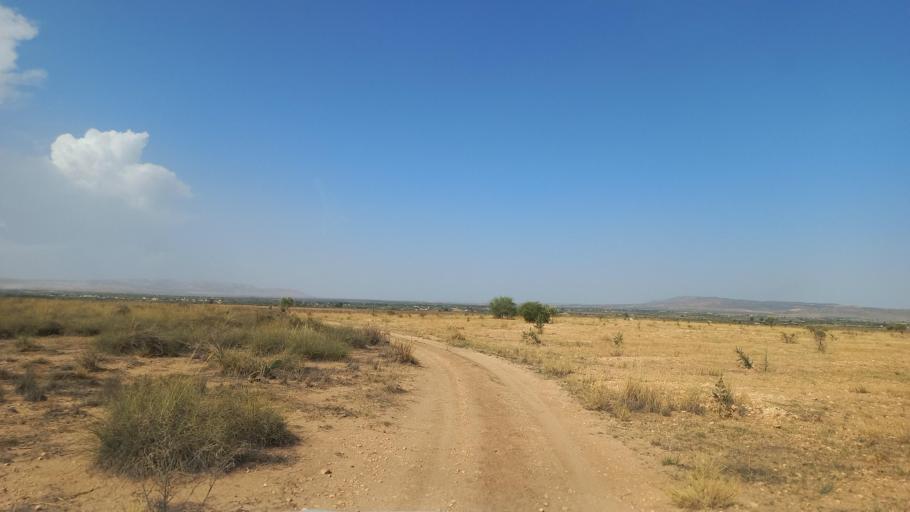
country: TN
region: Al Qasrayn
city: Kasserine
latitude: 35.2146
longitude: 9.0266
